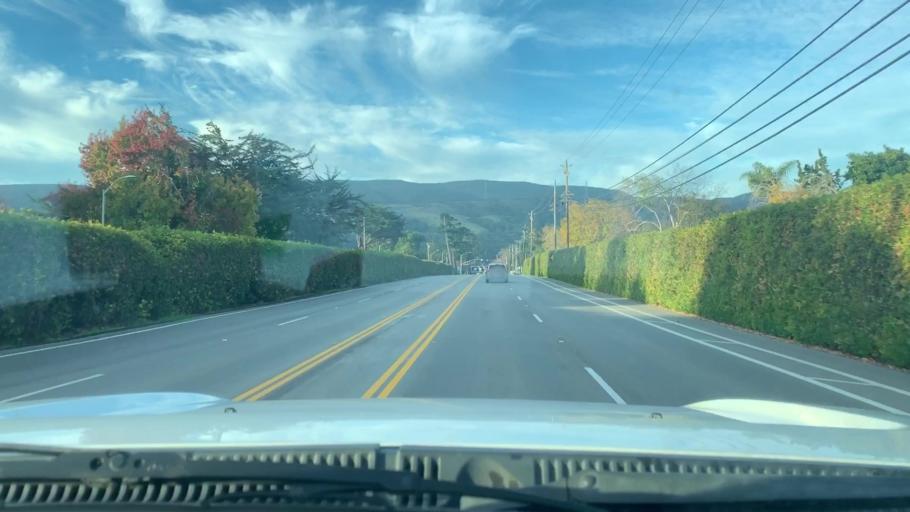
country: US
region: California
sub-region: San Luis Obispo County
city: San Luis Obispo
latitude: 35.2582
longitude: -120.6871
